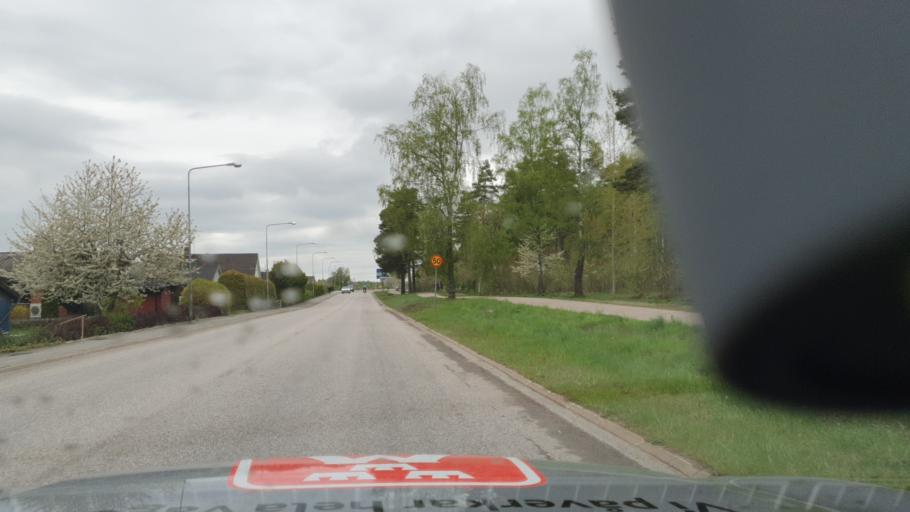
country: SE
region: Kalmar
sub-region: Vimmerby Kommun
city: Vimmerby
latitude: 57.6738
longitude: 15.8702
